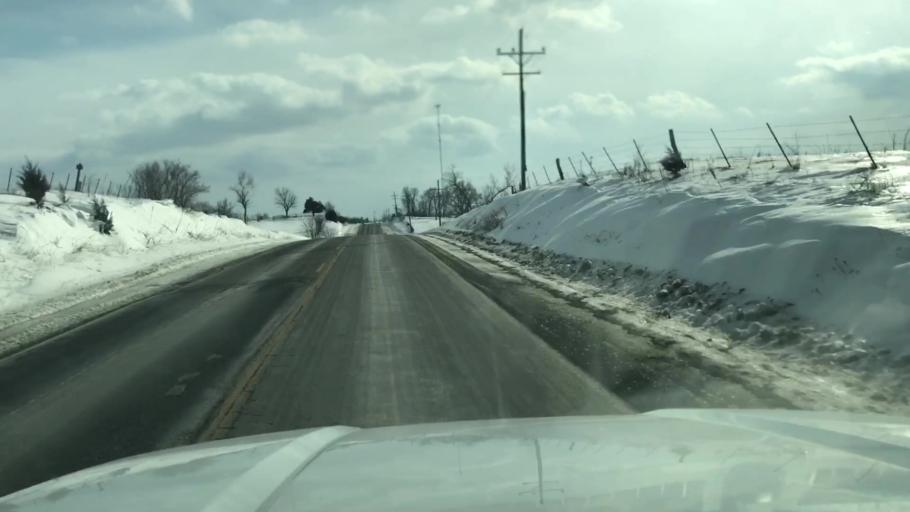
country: US
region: Missouri
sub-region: Gentry County
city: Stanberry
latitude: 40.3771
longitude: -94.6472
